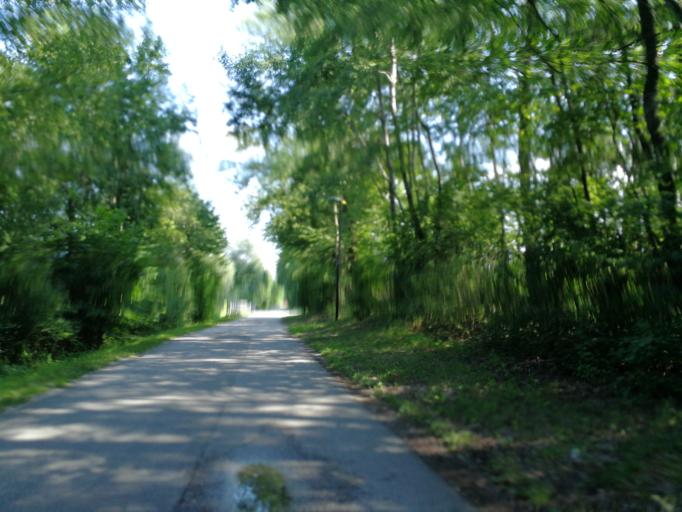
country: AT
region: Salzburg
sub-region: Politischer Bezirk Salzburg-Umgebung
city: Bergheim
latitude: 47.8313
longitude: 13.0271
